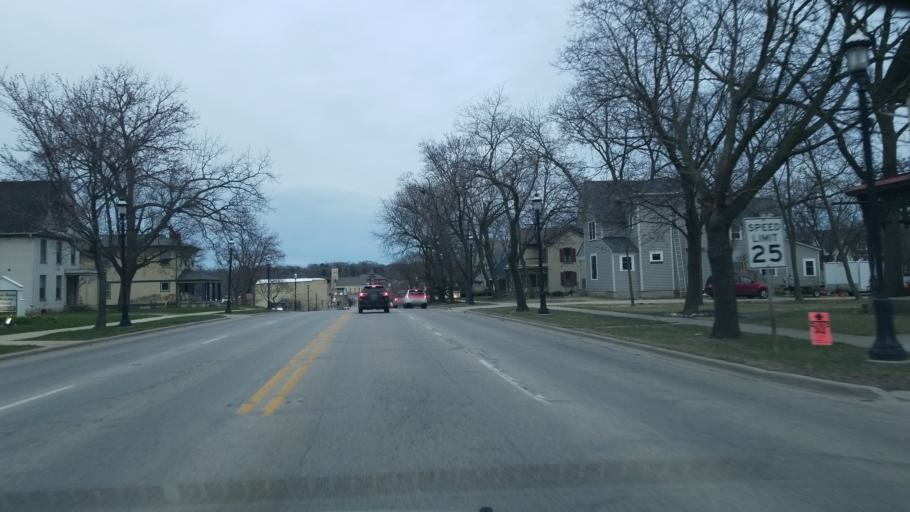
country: US
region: Illinois
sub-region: Kane County
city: West Dundee
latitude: 42.0981
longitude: -88.2812
